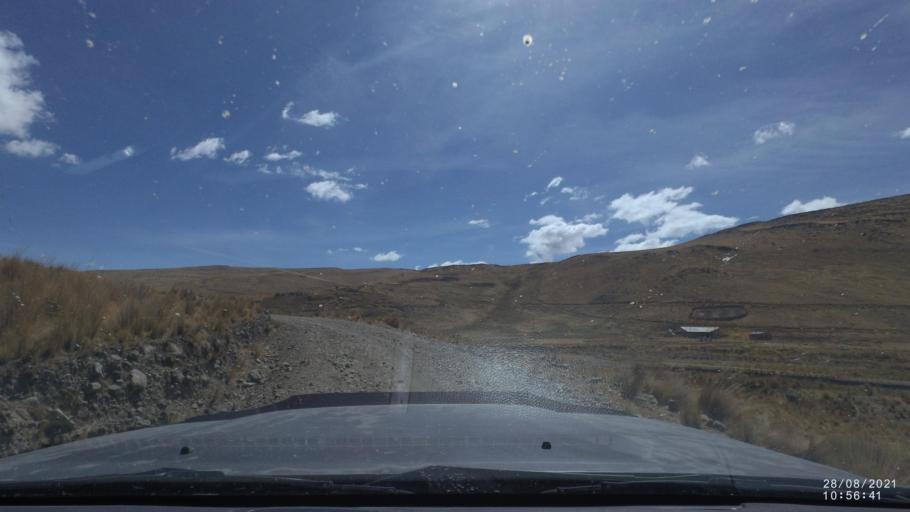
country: BO
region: Cochabamba
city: Cochabamba
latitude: -17.1920
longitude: -66.2496
